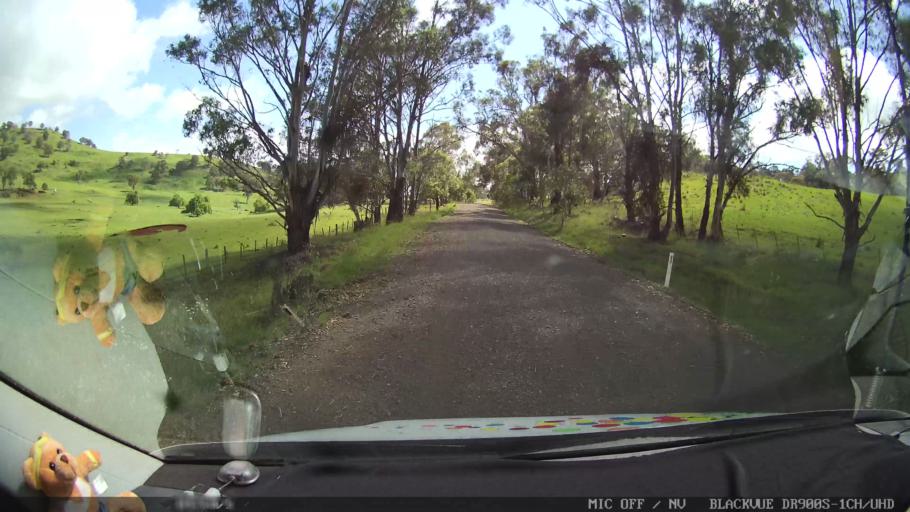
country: AU
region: New South Wales
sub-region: Guyra
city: Guyra
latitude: -29.9915
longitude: 151.6857
